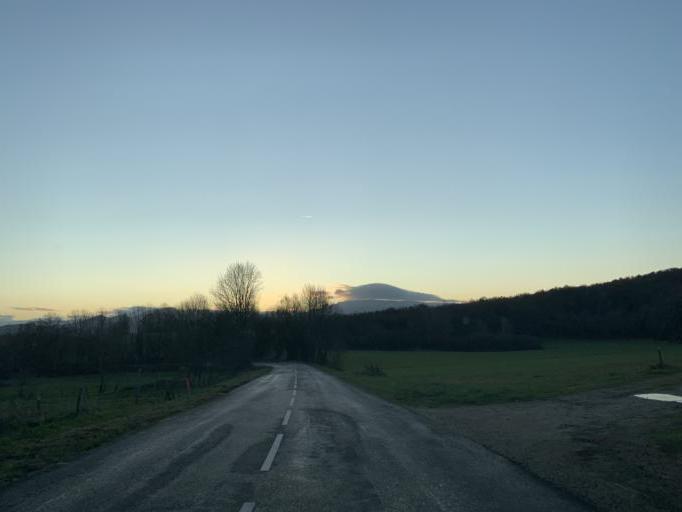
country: FR
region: Rhone-Alpes
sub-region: Departement de l'Ain
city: Belley
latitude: 45.7889
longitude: 5.6462
